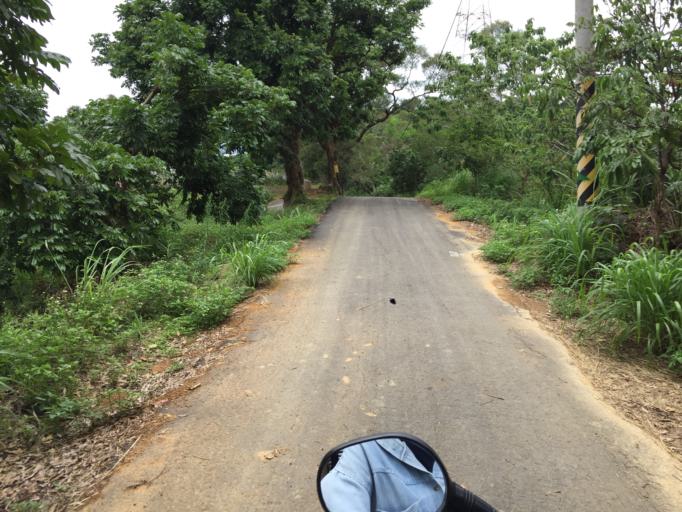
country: TW
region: Taiwan
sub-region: Taichung City
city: Taichung
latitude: 24.0660
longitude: 120.7144
